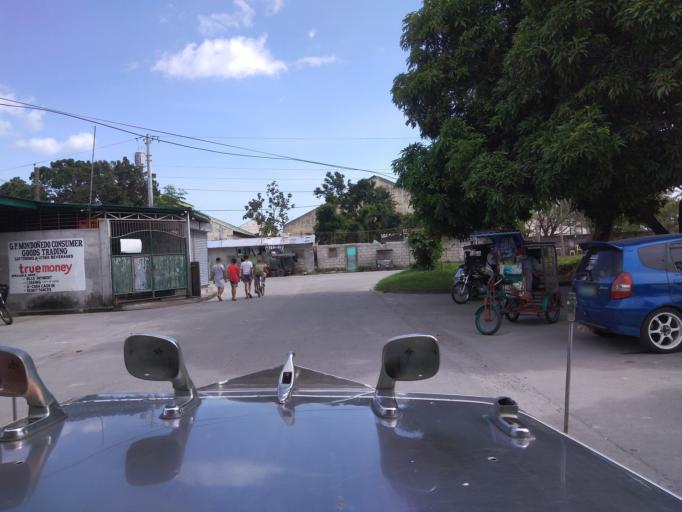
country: PH
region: Central Luzon
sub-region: Province of Pampanga
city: Pandacaqui
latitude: 15.1820
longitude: 120.6434
